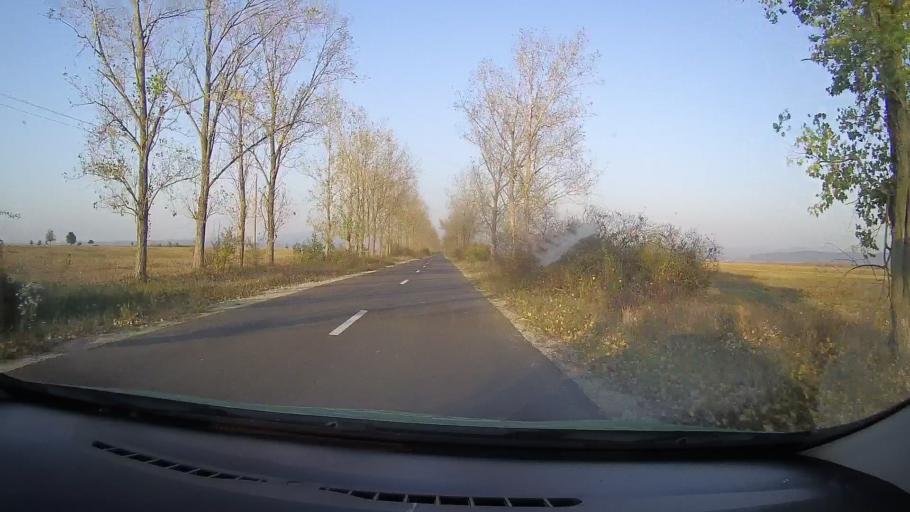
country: RO
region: Arad
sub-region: Comuna Barsa
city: Barsa
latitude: 46.3641
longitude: 22.0363
